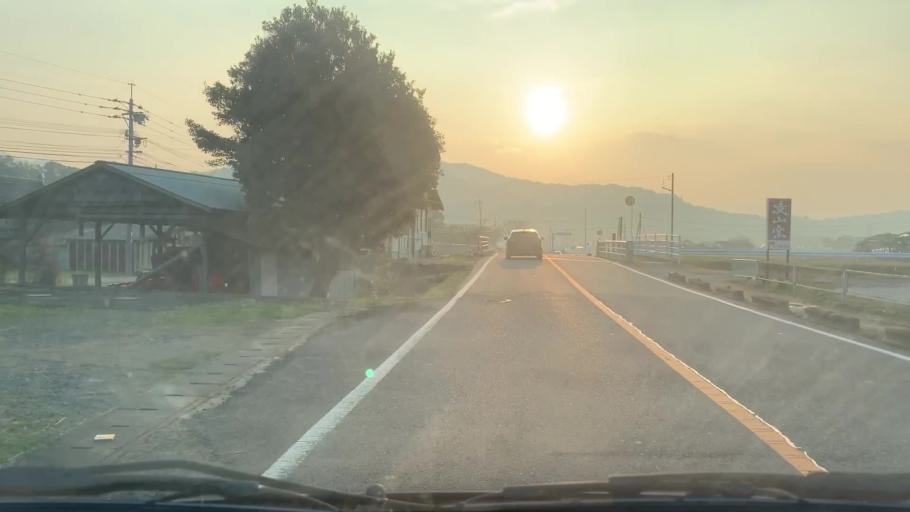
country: JP
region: Saga Prefecture
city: Takeocho-takeo
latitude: 33.2550
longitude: 130.0016
